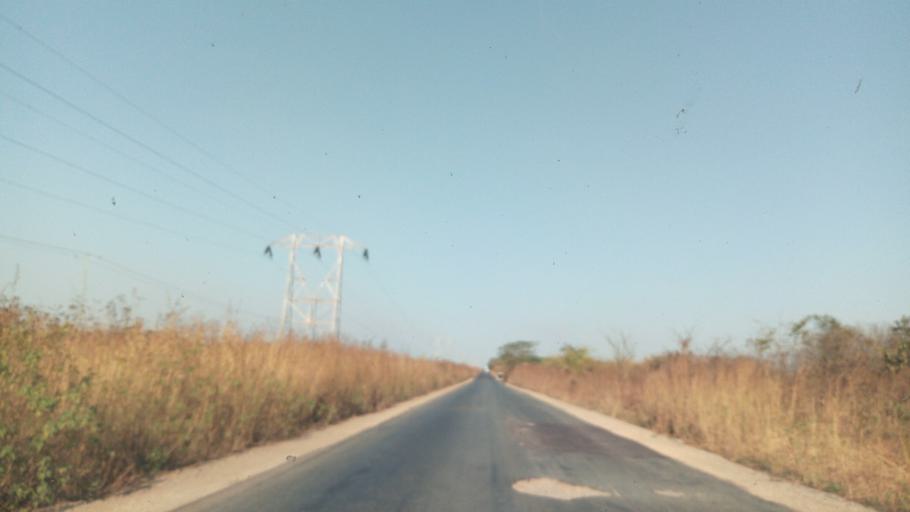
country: CD
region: Katanga
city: Likasi
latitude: -11.0015
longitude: 26.8955
